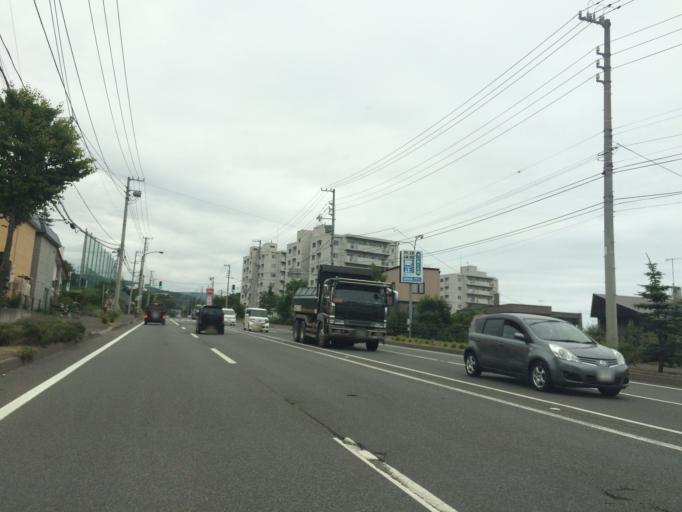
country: JP
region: Hokkaido
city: Otaru
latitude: 43.1397
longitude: 141.1578
